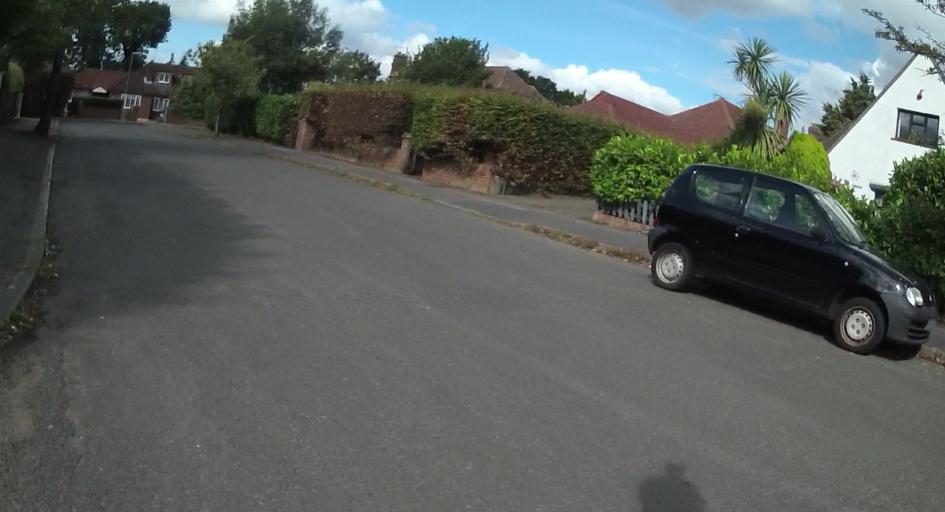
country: GB
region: England
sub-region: Surrey
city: Walton-on-Thames
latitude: 51.3809
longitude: -0.4012
